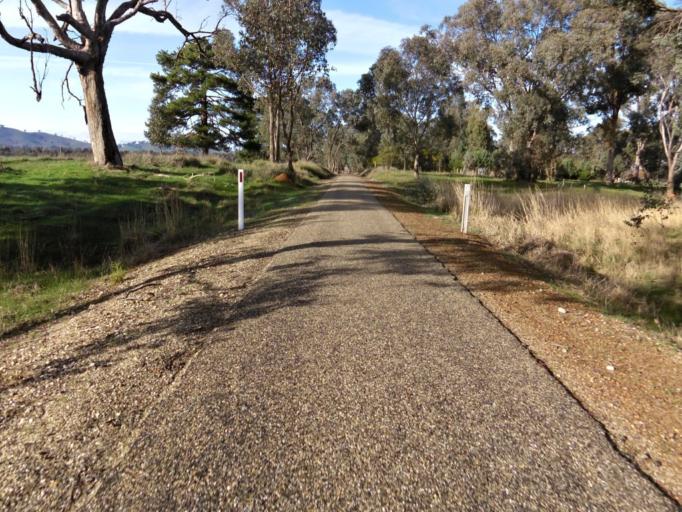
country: AU
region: Victoria
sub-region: Wangaratta
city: Wangaratta
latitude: -36.4155
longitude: 146.5500
